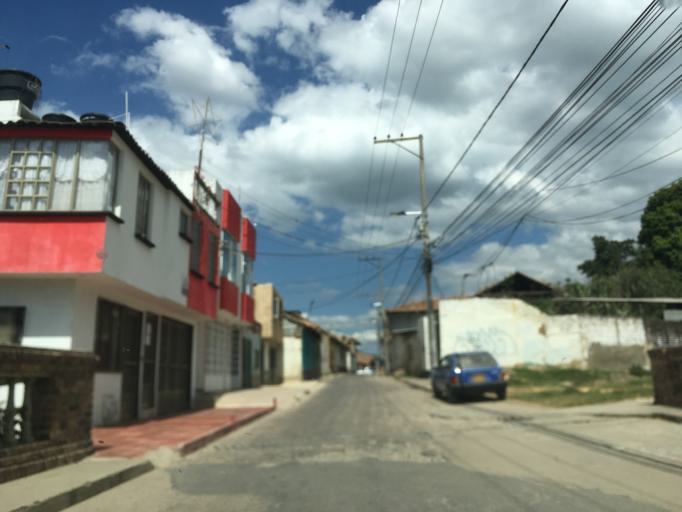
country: CO
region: Boyaca
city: Sogamoso
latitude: 5.7111
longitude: -72.9283
